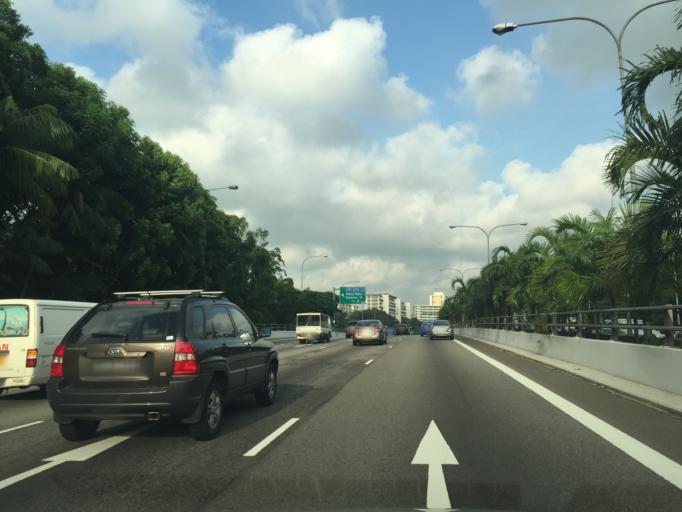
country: SG
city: Singapore
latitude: 1.3212
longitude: 103.8824
